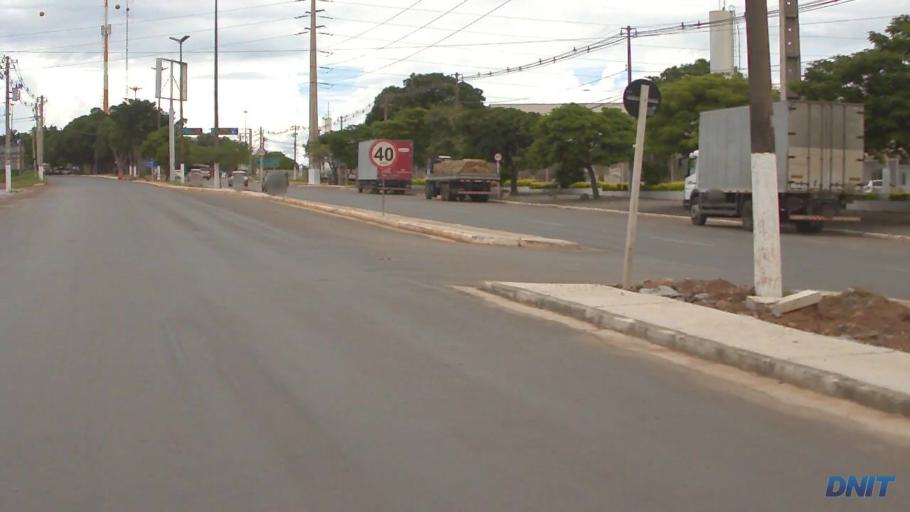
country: BR
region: Mato Grosso
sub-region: Varzea Grande
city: Varzea Grande
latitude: -15.6482
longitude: -56.1920
